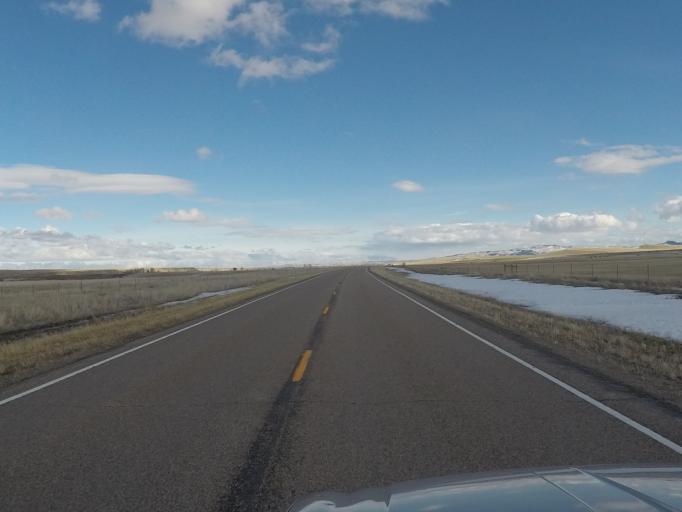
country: US
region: Montana
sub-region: Wheatland County
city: Harlowton
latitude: 46.4945
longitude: -110.3374
